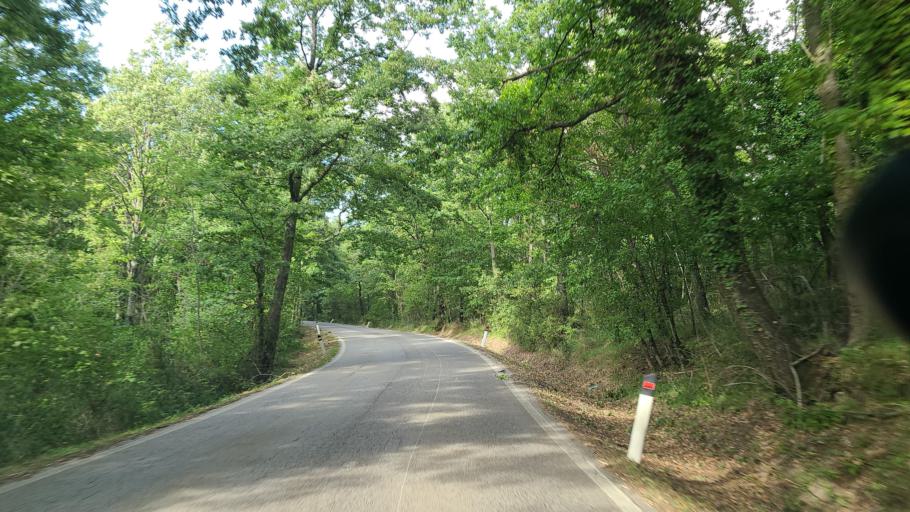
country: IT
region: Tuscany
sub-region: Provincia di Siena
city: San Gimignano
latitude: 43.4311
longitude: 10.9682
